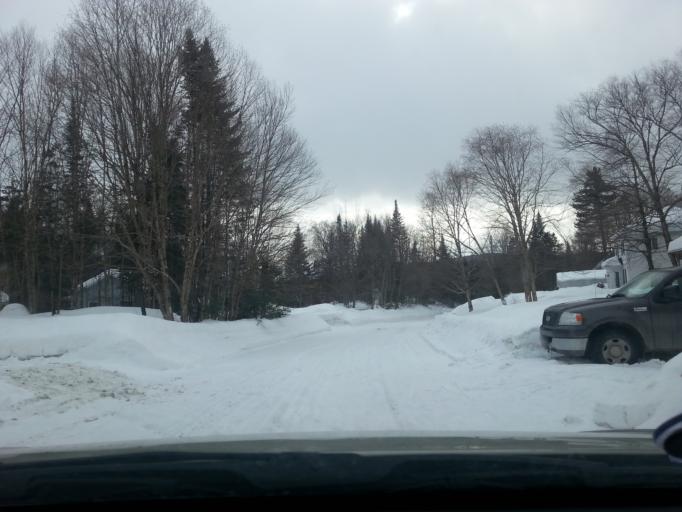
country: CA
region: Quebec
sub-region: Capitale-Nationale
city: Shannon
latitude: 46.9954
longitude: -71.3893
